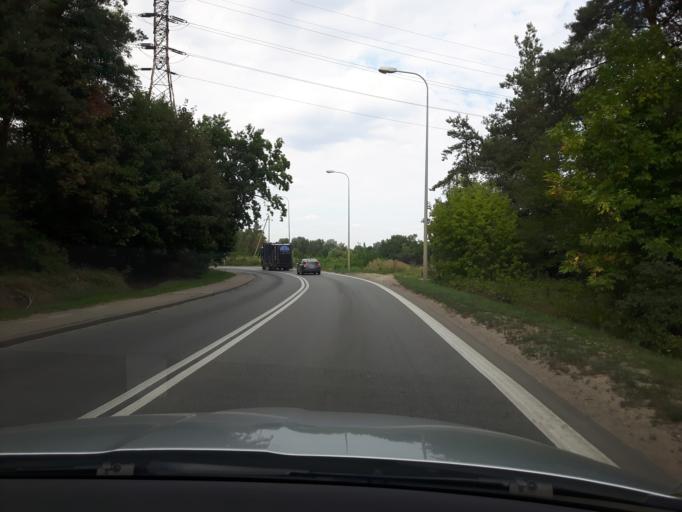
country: PL
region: Masovian Voivodeship
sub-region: Warszawa
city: Targowek
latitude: 52.3295
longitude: 21.0305
